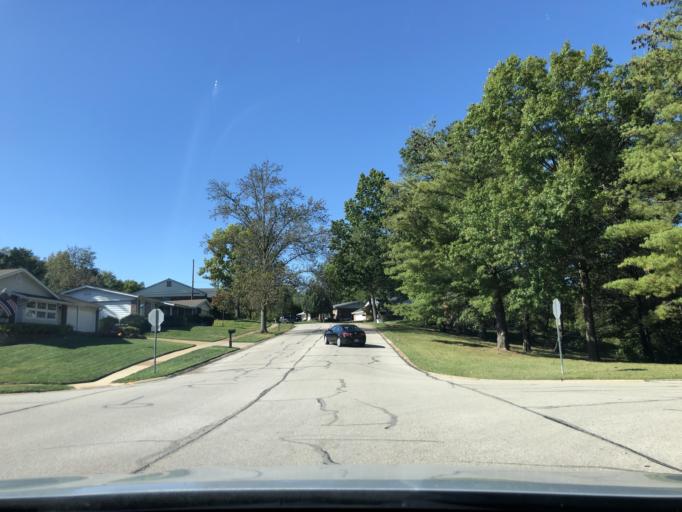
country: US
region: Missouri
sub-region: Saint Louis County
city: Concord
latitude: 38.4994
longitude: -90.3705
